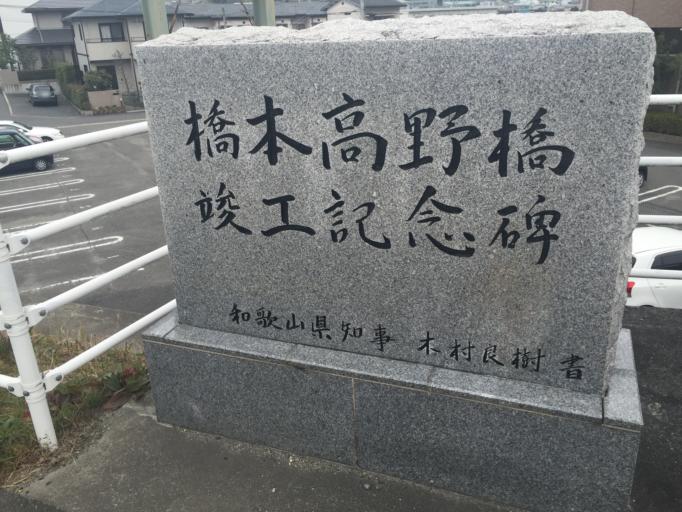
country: JP
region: Wakayama
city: Hashimoto
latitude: 34.3109
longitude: 135.6016
